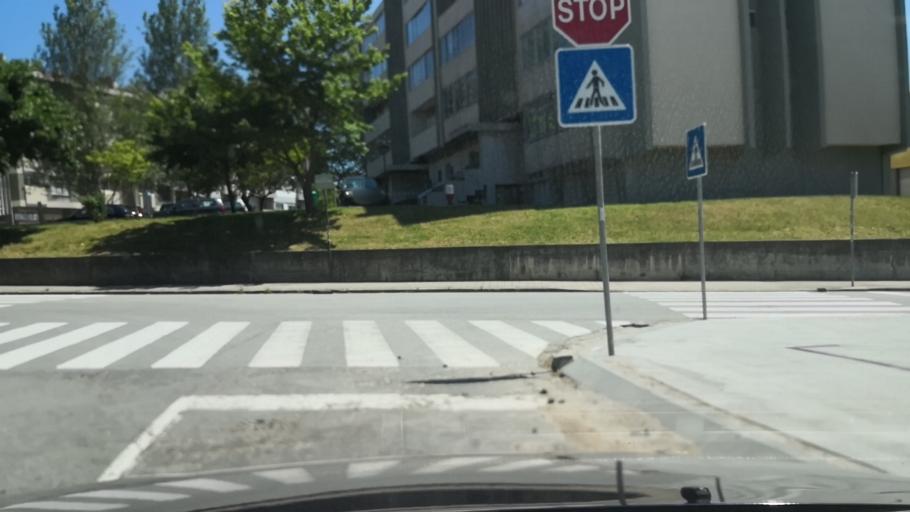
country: PT
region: Porto
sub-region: Vila Nova de Gaia
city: Canidelo
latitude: 41.1496
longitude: -8.6608
